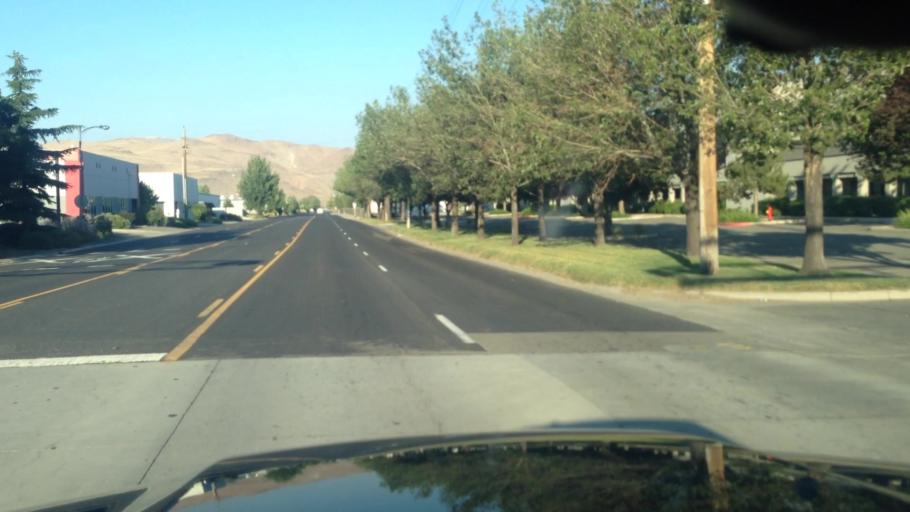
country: US
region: Nevada
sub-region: Washoe County
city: Sparks
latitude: 39.5213
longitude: -119.7318
